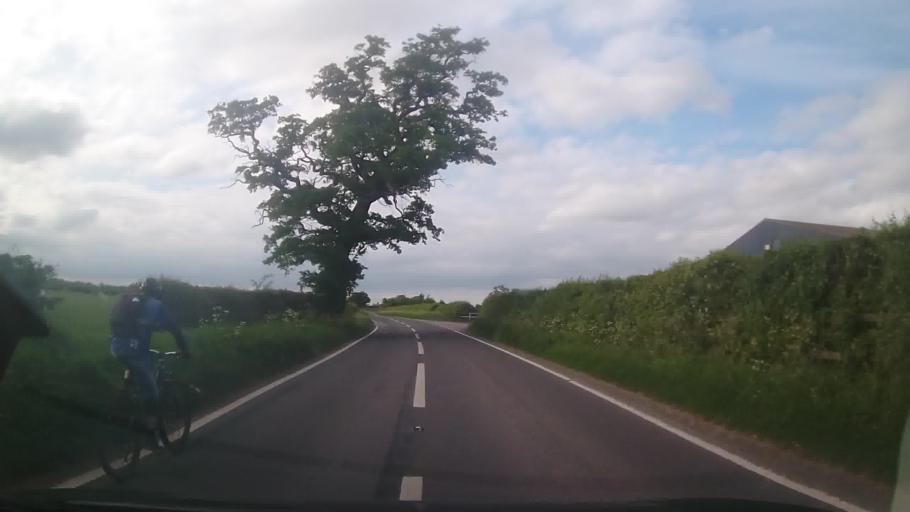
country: GB
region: England
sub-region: Shropshire
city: Petton
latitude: 52.8143
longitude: -2.7900
